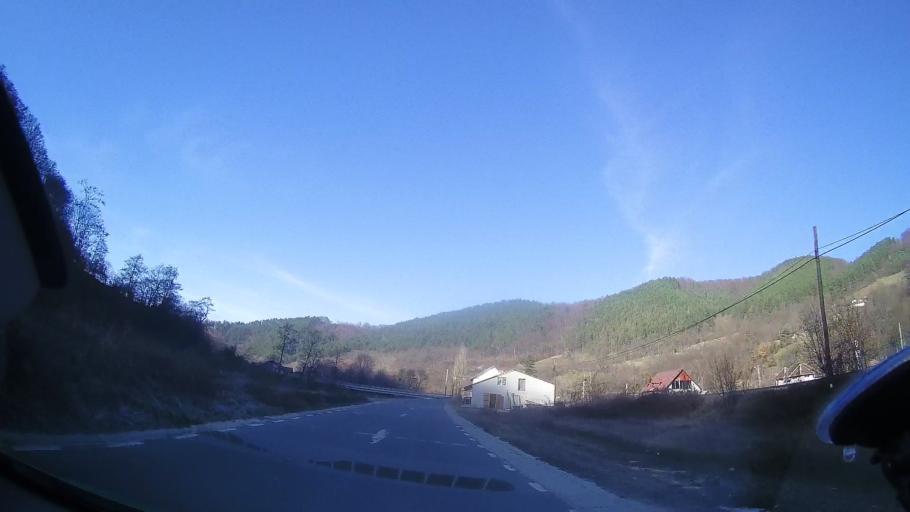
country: RO
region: Bihor
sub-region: Comuna Bratca
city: Bratca
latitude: 46.9260
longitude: 22.6489
